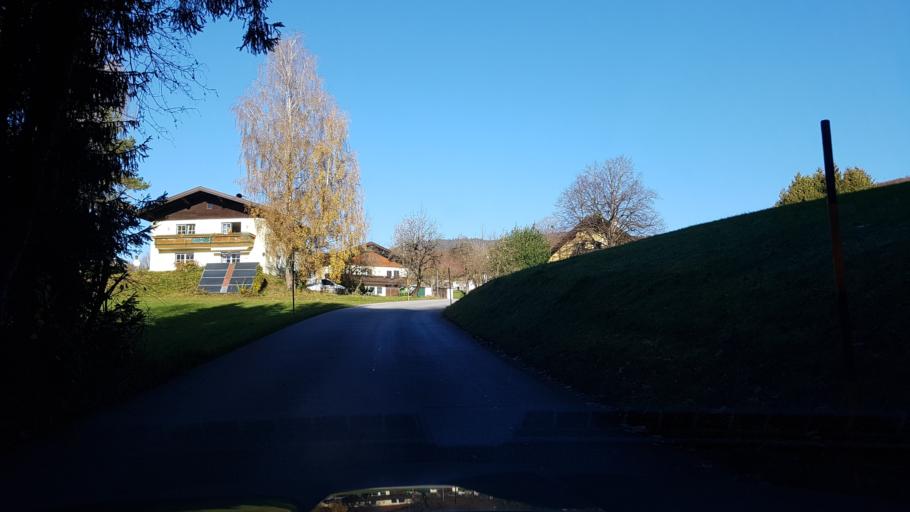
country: AT
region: Salzburg
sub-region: Politischer Bezirk Hallein
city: Puch bei Hallein
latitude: 47.7256
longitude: 13.1005
